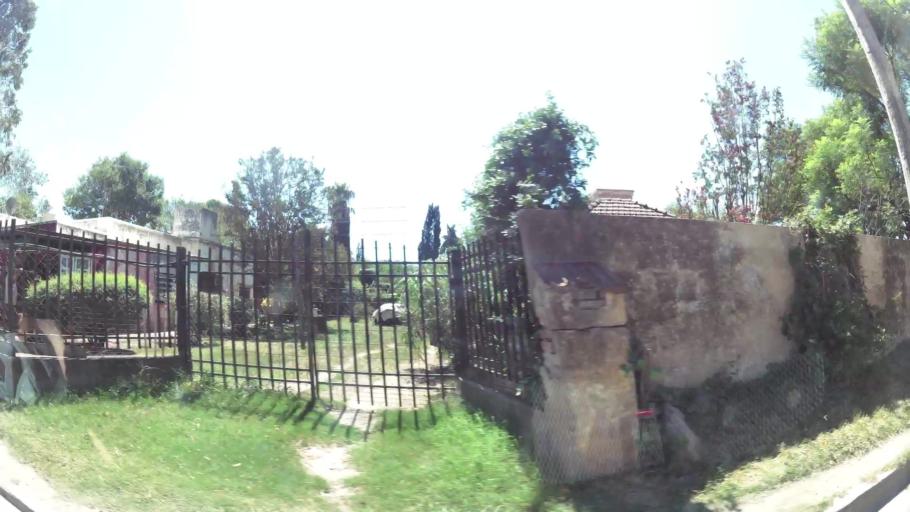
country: AR
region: Cordoba
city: Saldan
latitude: -31.3374
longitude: -64.2856
